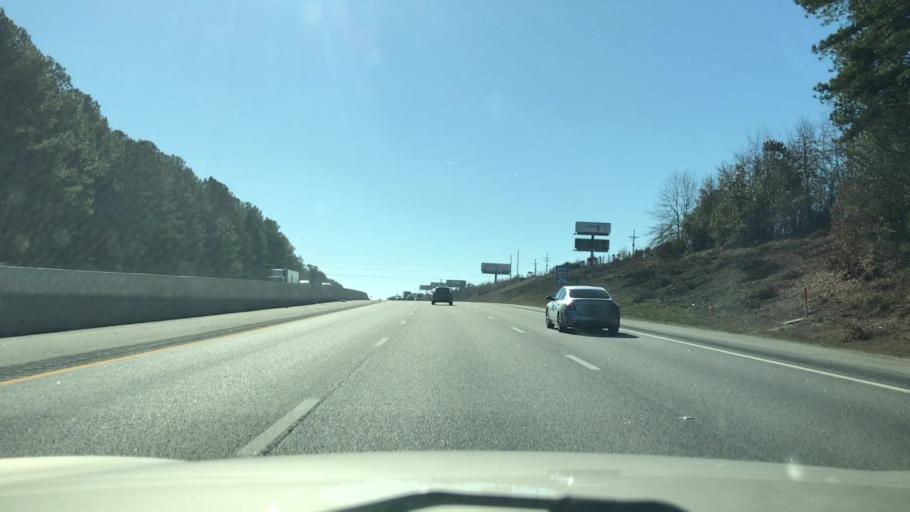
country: US
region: South Carolina
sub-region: Lexington County
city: Pineridge
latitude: 33.8742
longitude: -81.0360
